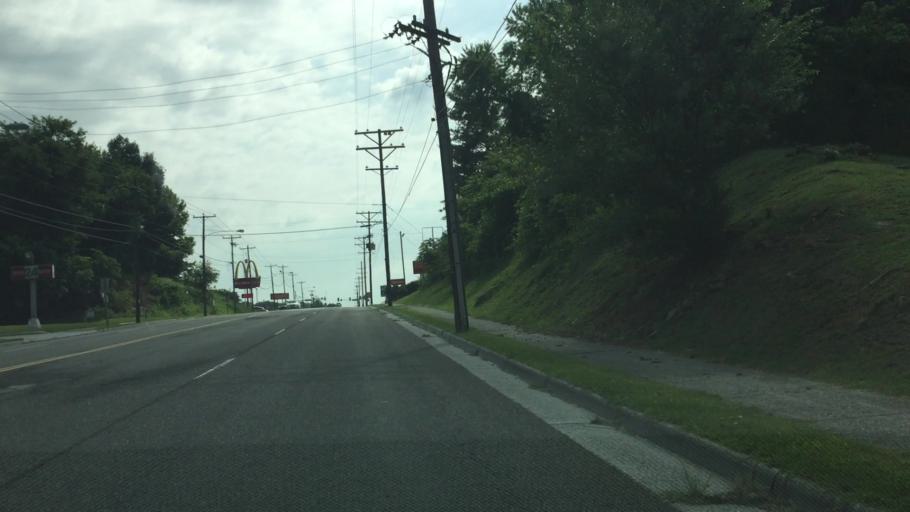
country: US
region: Virginia
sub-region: Pulaski County
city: Pulaski
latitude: 37.0485
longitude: -80.7653
